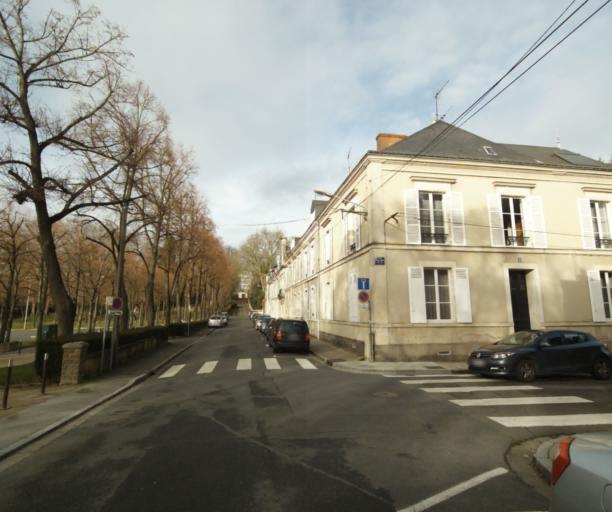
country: FR
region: Pays de la Loire
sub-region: Departement de la Sarthe
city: Le Mans
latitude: 48.0082
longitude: 0.2036
